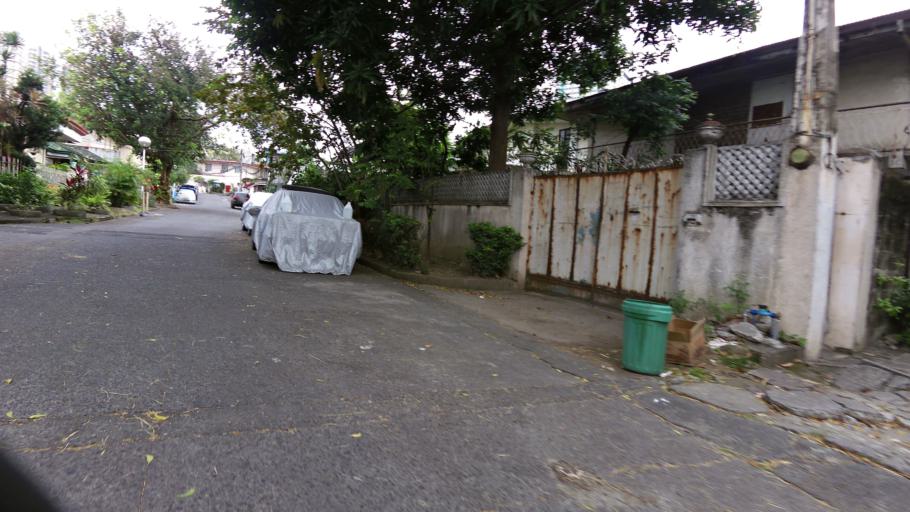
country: PH
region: Metro Manila
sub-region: Pasig
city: Pasig City
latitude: 14.5694
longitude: 121.0624
